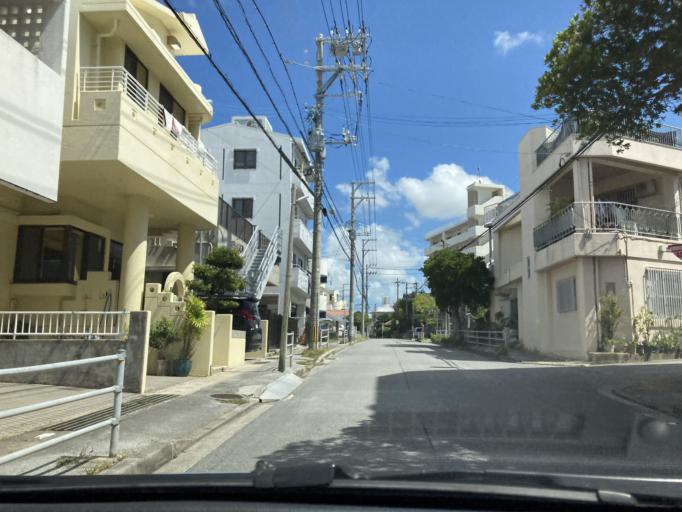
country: JP
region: Okinawa
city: Tomigusuku
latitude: 26.1938
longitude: 127.6687
